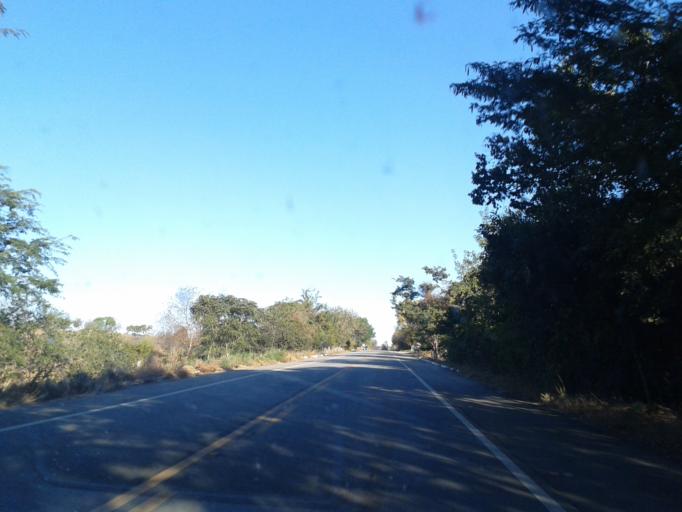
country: BR
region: Goias
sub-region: Itapuranga
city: Itapuranga
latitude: -15.6247
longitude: -50.2349
